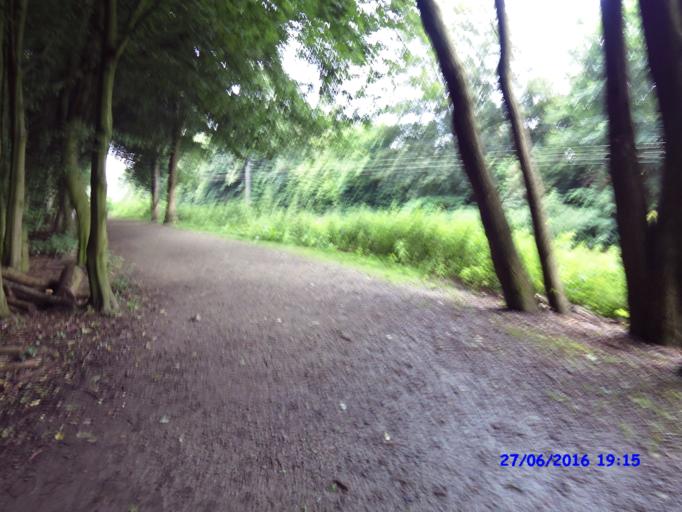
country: BE
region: Flanders
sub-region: Provincie Vlaams-Brabant
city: Wemmel
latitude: 50.8817
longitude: 4.3046
